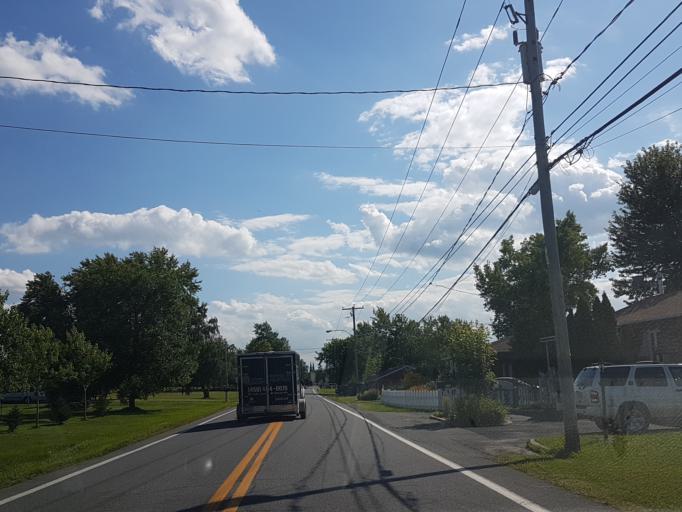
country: CA
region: Quebec
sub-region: Monteregie
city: Saint-Denis-sur-Richelieu
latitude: 45.7952
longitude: -73.1536
